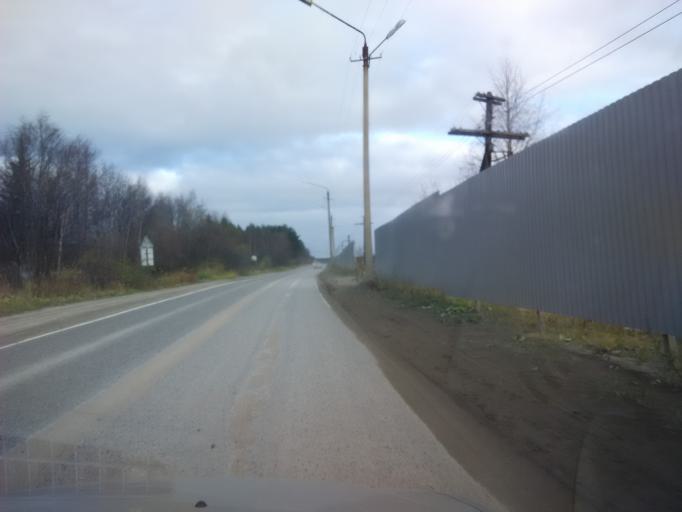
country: RU
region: Murmansk
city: Polyarnyye Zori
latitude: 67.3807
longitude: 32.5093
